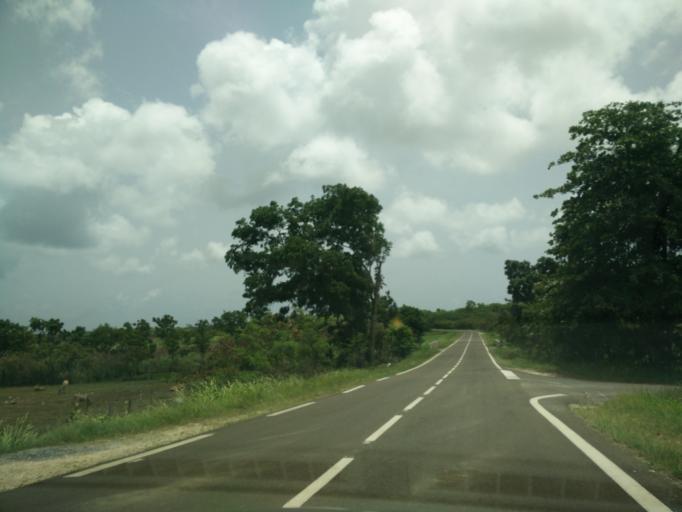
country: GP
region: Guadeloupe
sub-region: Guadeloupe
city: Port-Louis
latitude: 16.4368
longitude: -61.5125
